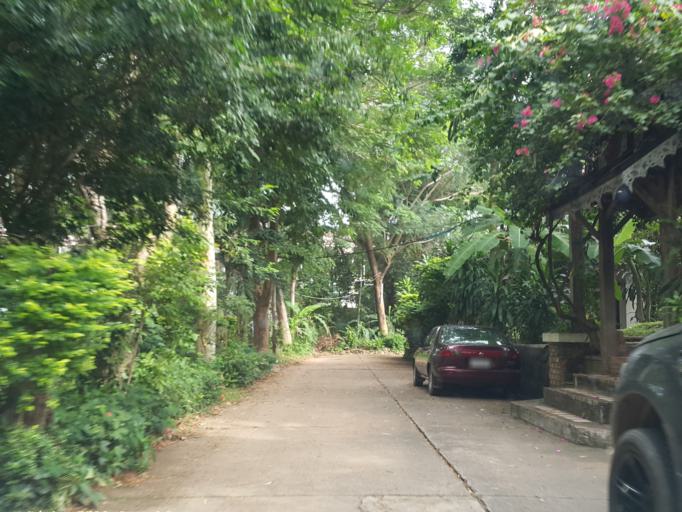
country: TH
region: Mae Hong Son
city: Mae Hong Son
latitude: 19.2942
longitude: 97.9637
